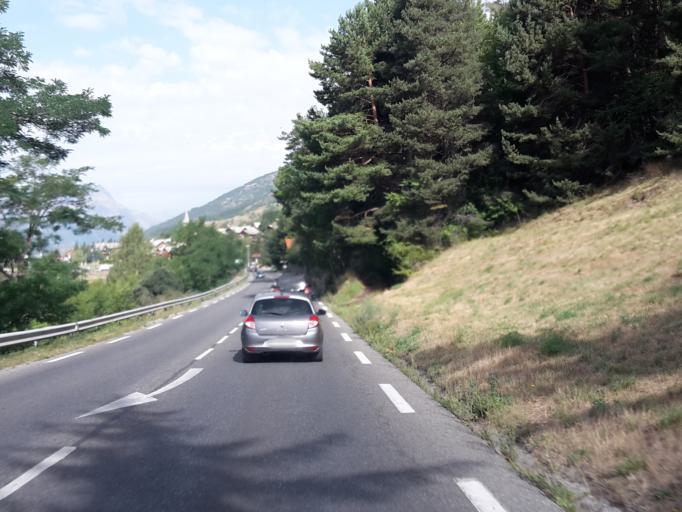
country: FR
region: Provence-Alpes-Cote d'Azur
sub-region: Departement des Hautes-Alpes
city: Saint-Chaffrey
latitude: 44.9198
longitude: 6.6183
